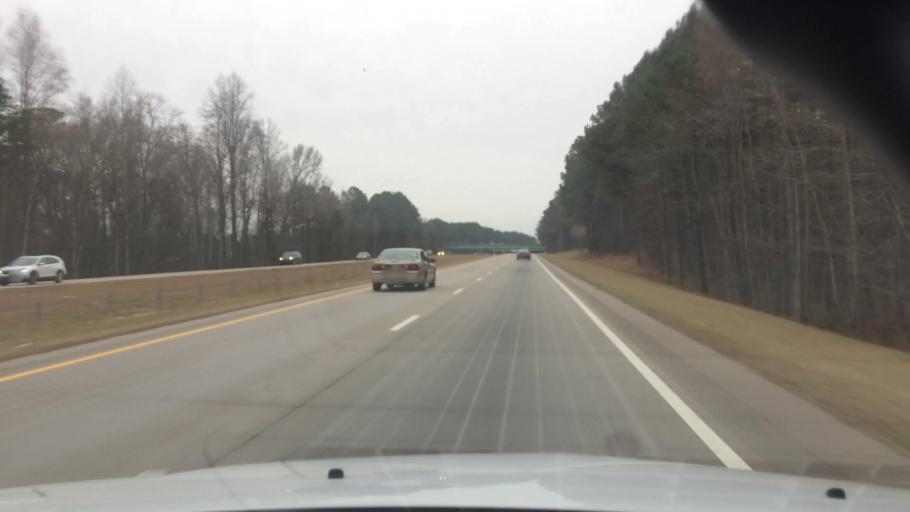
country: US
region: North Carolina
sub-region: Wake County
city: Zebulon
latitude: 35.8403
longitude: -78.2980
